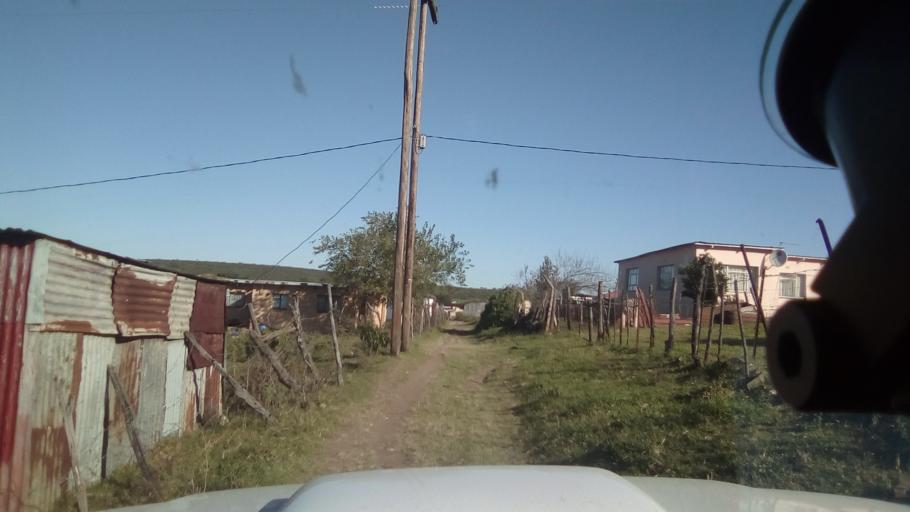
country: ZA
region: Eastern Cape
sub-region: Buffalo City Metropolitan Municipality
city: Bhisho
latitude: -32.7984
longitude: 27.3411
